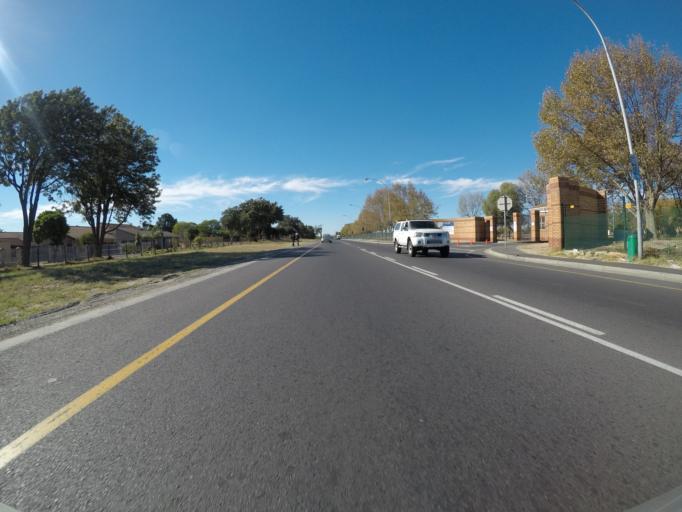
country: ZA
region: Western Cape
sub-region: City of Cape Town
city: Kraaifontein
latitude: -33.9405
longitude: 18.6768
